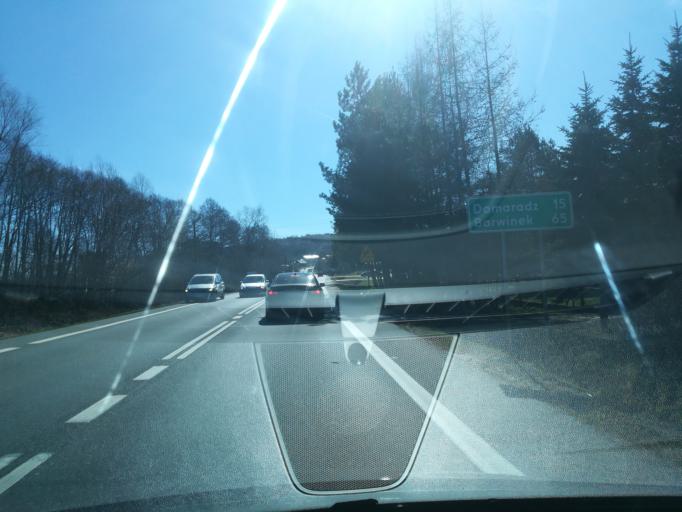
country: PL
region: Subcarpathian Voivodeship
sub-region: Powiat strzyzowski
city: Niebylec
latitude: 49.8621
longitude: 21.9031
